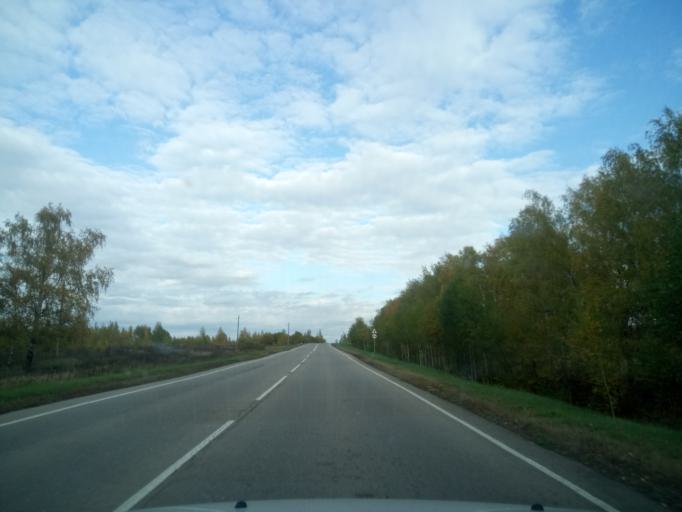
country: RU
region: Nizjnij Novgorod
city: Bol'shoye Boldino
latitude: 54.9217
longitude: 45.1403
